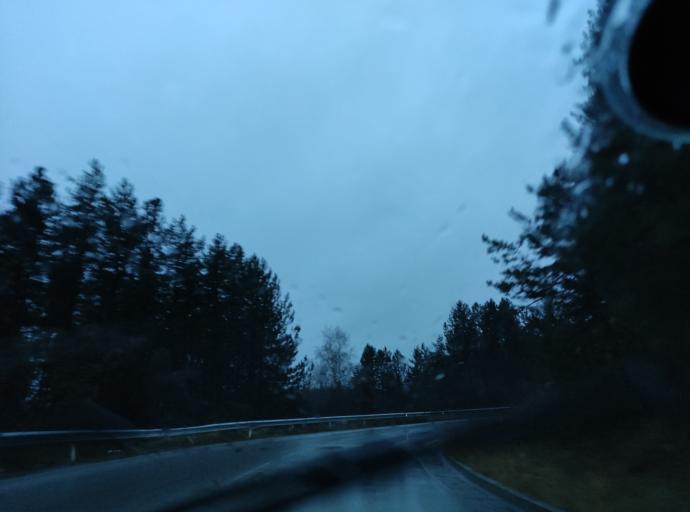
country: BG
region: Sofia-Capital
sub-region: Stolichna Obshtina
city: Sofia
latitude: 42.5502
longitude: 23.3670
